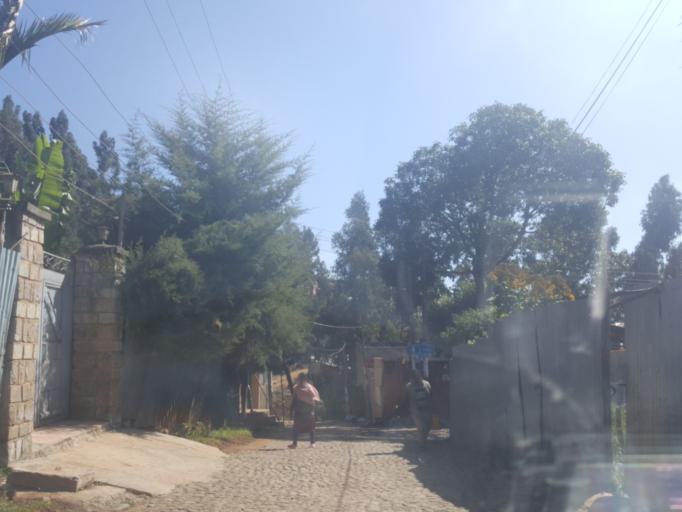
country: ET
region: Adis Abeba
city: Addis Ababa
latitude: 9.0687
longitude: 38.7280
